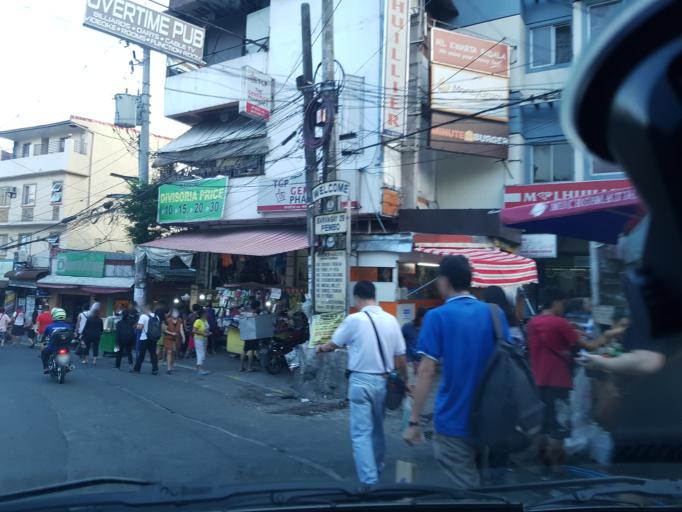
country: PH
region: Calabarzon
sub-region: Province of Rizal
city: Pateros
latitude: 14.5457
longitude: 121.0560
